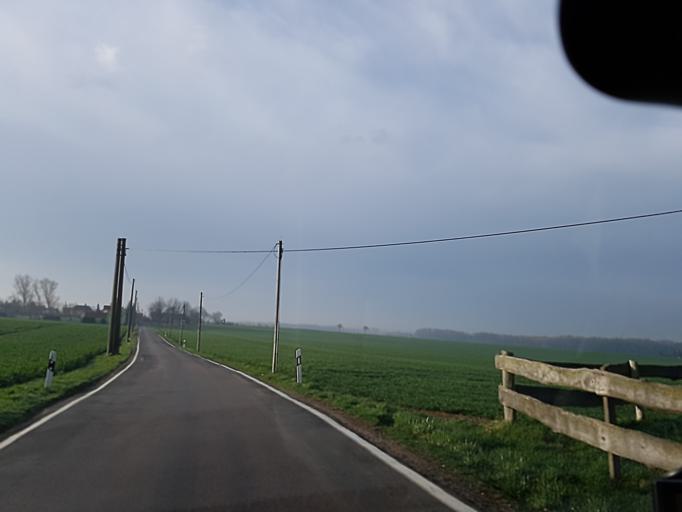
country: DE
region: Saxony
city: Stauchitz
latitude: 51.2755
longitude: 13.1936
